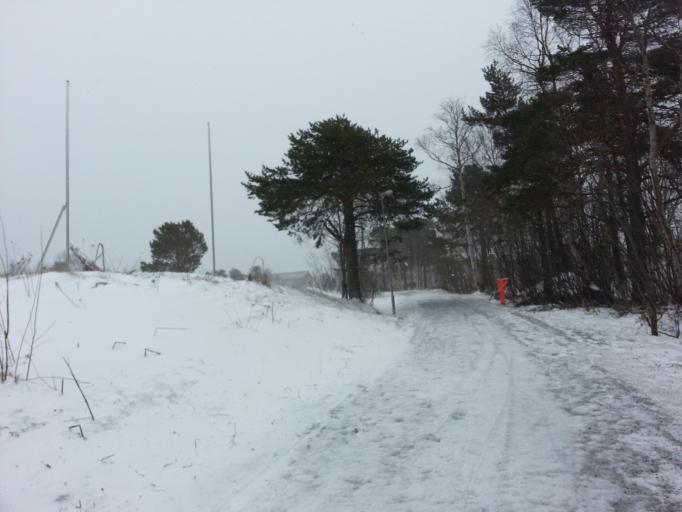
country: NO
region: Sor-Trondelag
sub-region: Oppdal
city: Oppdal
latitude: 62.5959
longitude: 9.6827
